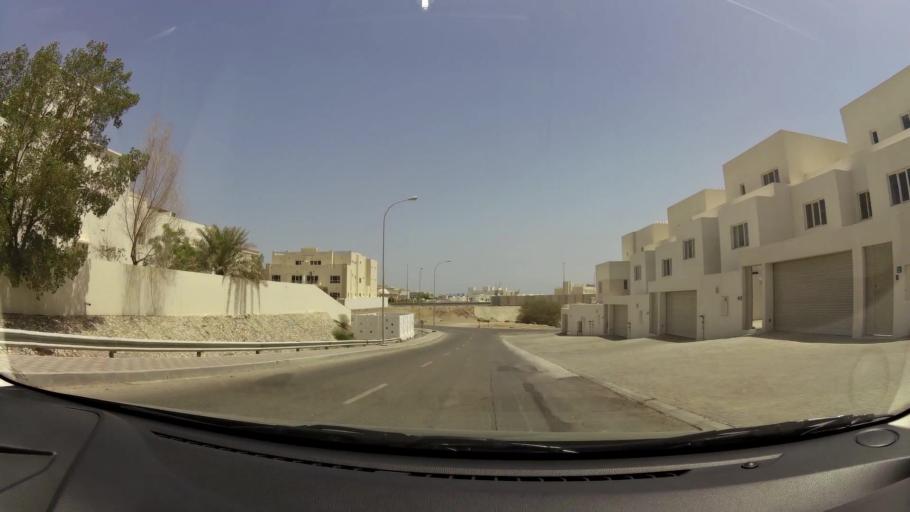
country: OM
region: Muhafazat Masqat
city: Bawshar
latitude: 23.5885
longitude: 58.4560
